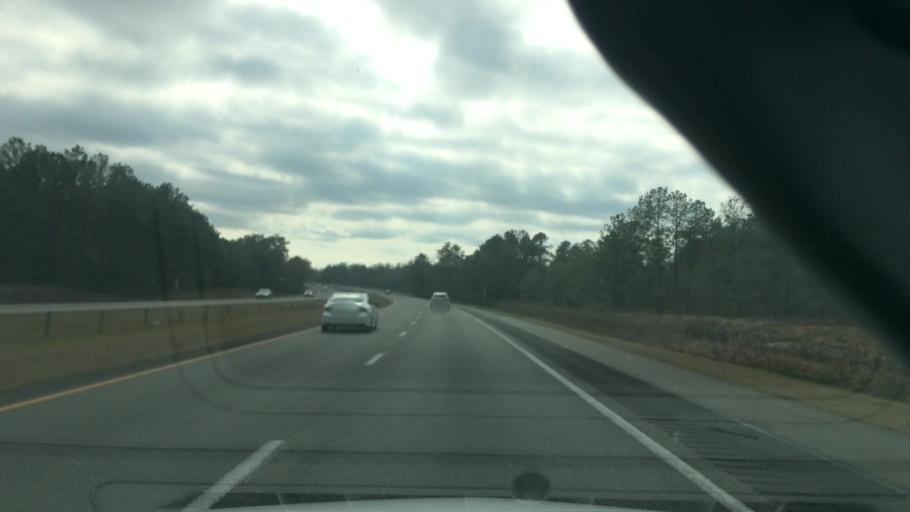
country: US
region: North Carolina
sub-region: New Hanover County
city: Castle Hayne
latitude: 34.3732
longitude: -77.8860
